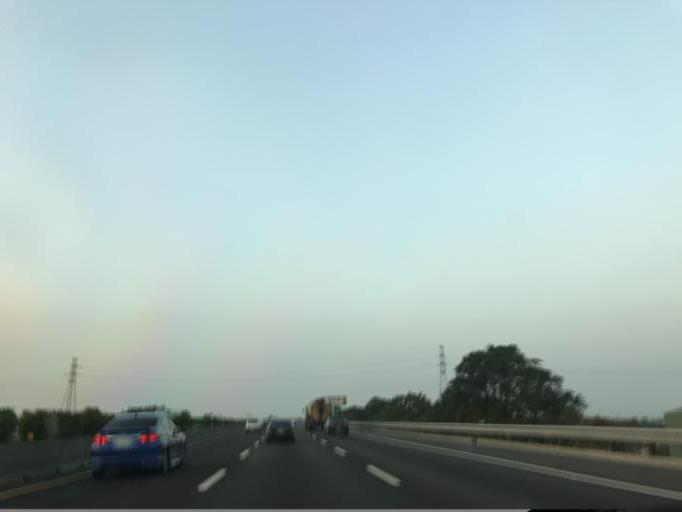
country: TW
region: Taiwan
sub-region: Yunlin
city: Douliu
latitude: 23.7172
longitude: 120.4760
